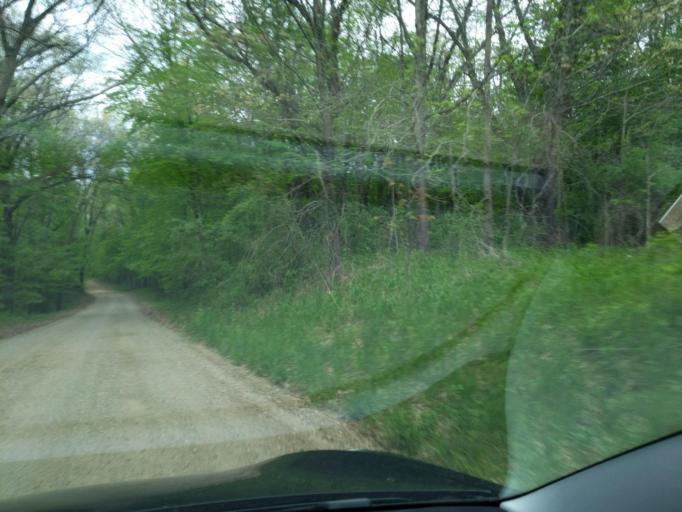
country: US
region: Michigan
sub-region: Ingham County
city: Stockbridge
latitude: 42.5234
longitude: -84.2948
